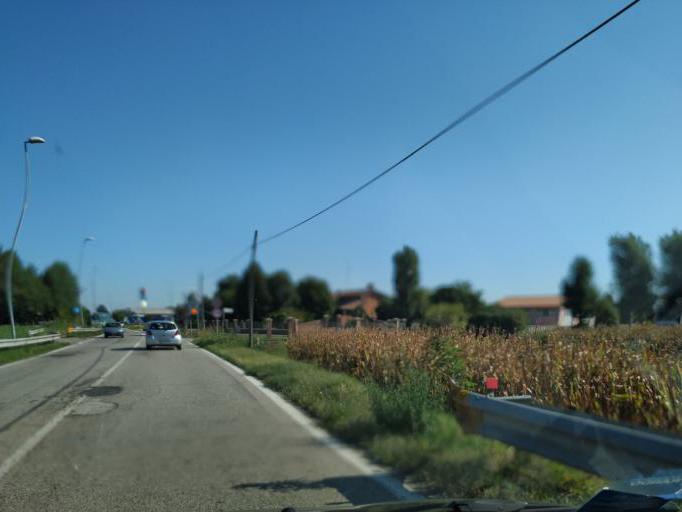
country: IT
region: Emilia-Romagna
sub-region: Provincia di Bologna
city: Decima
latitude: 44.6962
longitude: 11.2245
